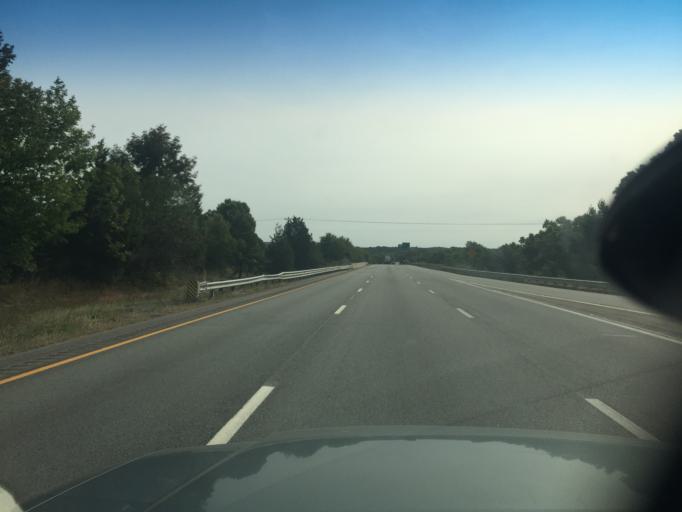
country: US
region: Massachusetts
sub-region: Norfolk County
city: Wrentham
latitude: 42.0372
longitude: -71.3088
